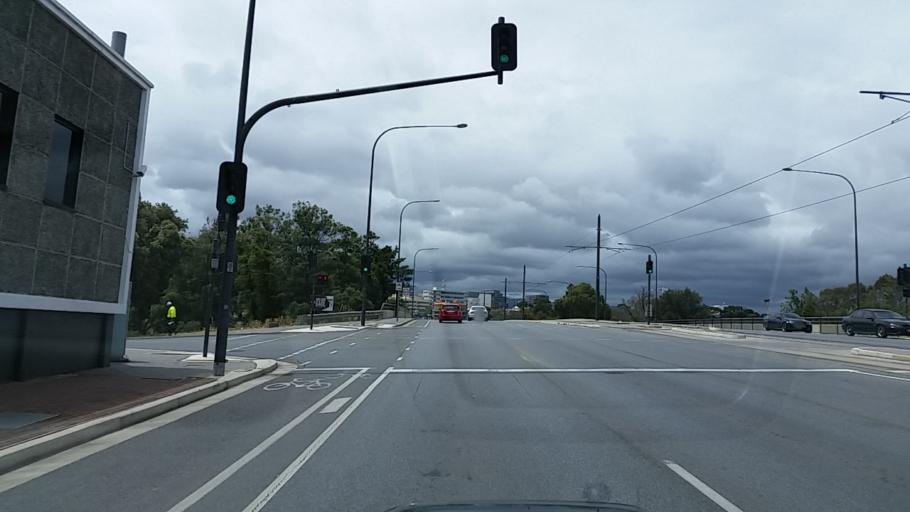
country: AU
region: South Australia
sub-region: City of West Torrens
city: Thebarton
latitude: -34.9198
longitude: 138.5817
